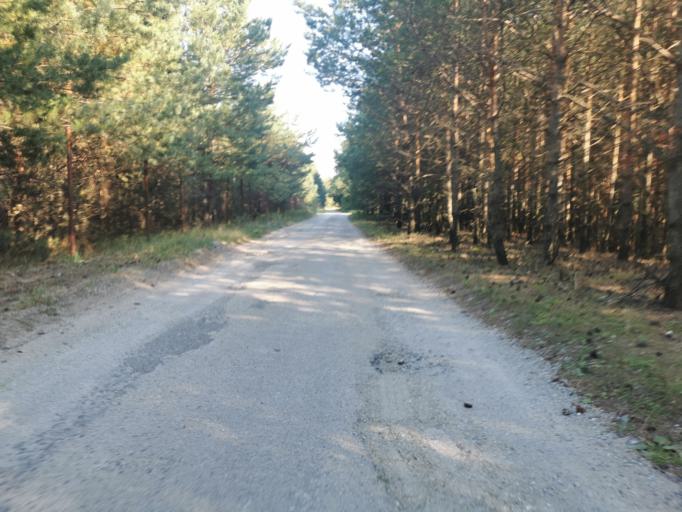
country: SK
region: Trnavsky
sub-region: Okres Senica
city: Senica
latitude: 48.6570
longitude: 17.2922
